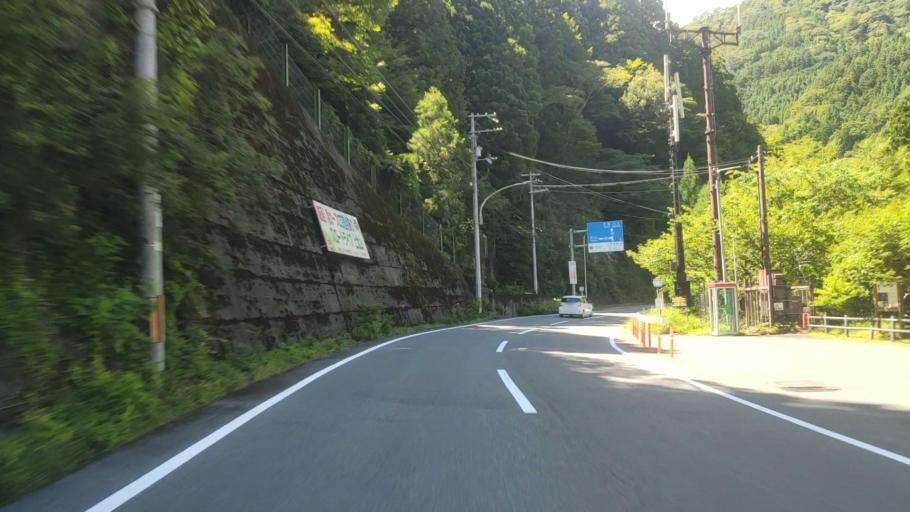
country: JP
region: Mie
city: Owase
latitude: 34.1907
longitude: 135.9936
